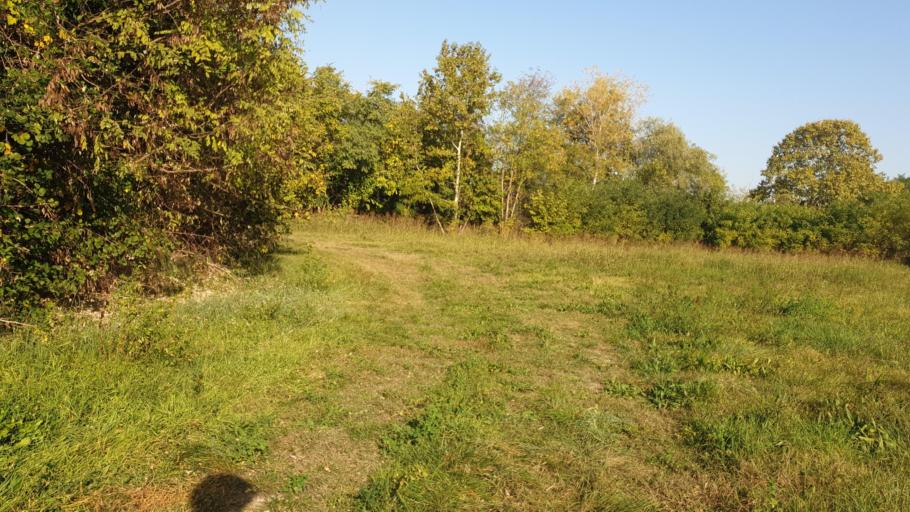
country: IT
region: Veneto
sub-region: Provincia di Venezia
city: Galta
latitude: 45.3975
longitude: 12.0165
